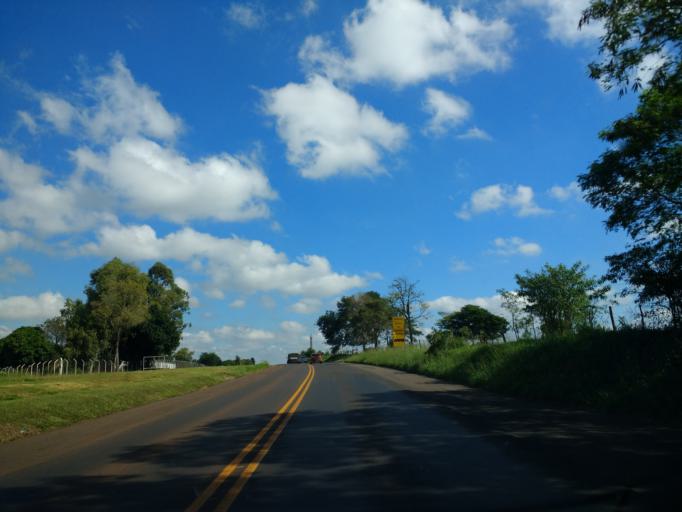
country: BR
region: Parana
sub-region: Umuarama
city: Umuarama
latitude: -23.8313
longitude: -53.3539
